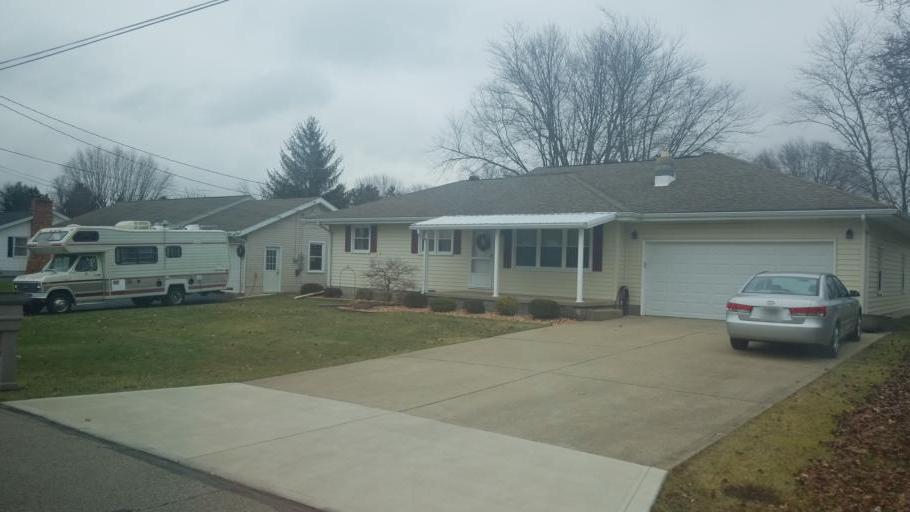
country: US
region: Ohio
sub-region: Crawford County
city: Galion
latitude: 40.7238
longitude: -82.8043
